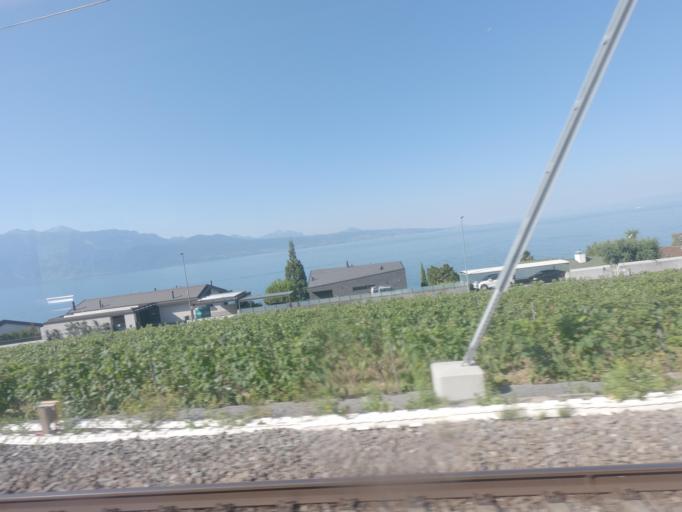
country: CH
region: Vaud
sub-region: Lavaux-Oron District
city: Cully
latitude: 46.4899
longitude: 6.7170
